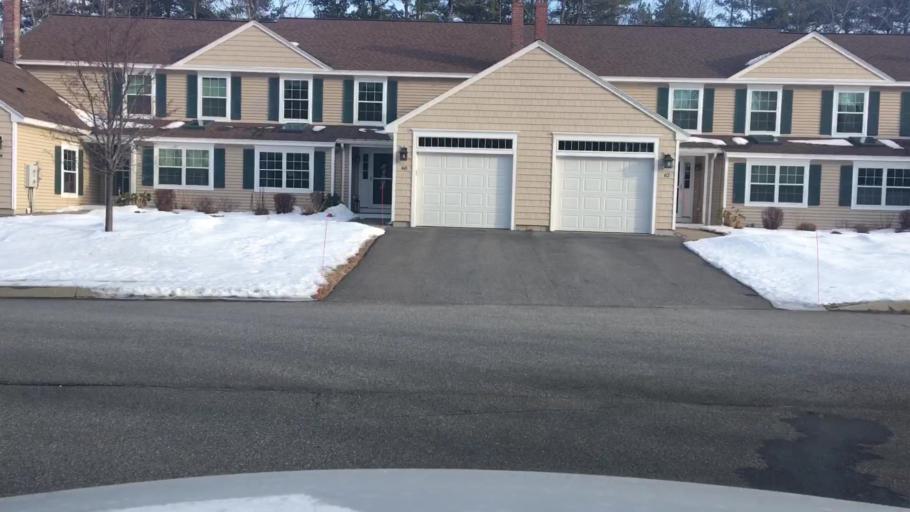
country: US
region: Maine
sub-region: York County
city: Wells Beach Station
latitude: 43.3520
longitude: -70.5683
